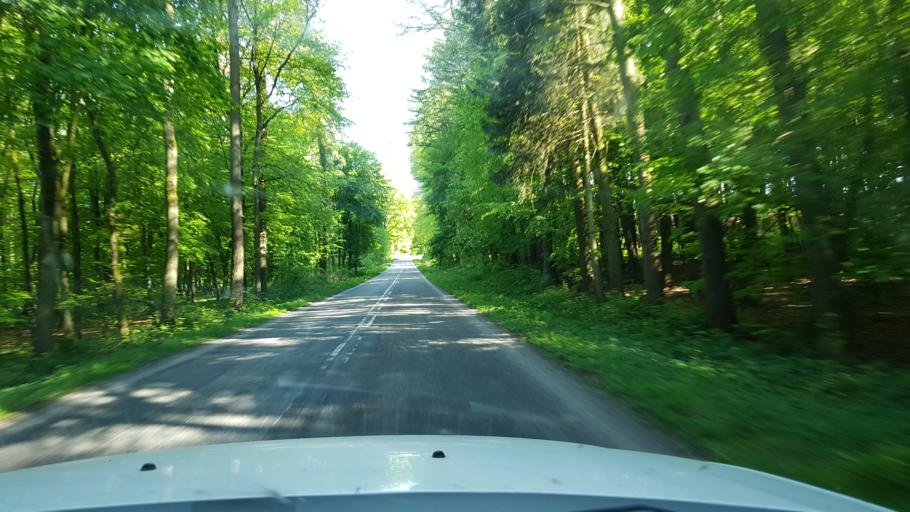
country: PL
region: West Pomeranian Voivodeship
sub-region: Powiat lobeski
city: Resko
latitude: 53.8357
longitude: 15.3830
